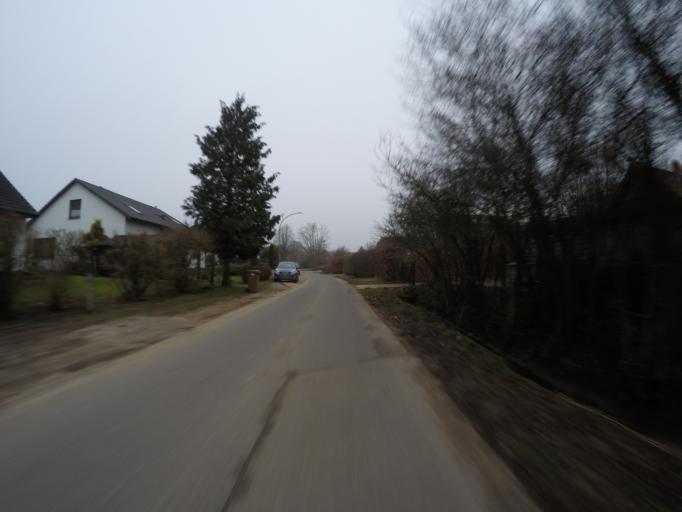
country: DE
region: Schleswig-Holstein
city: Quickborn
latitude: 53.7204
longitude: 9.8603
